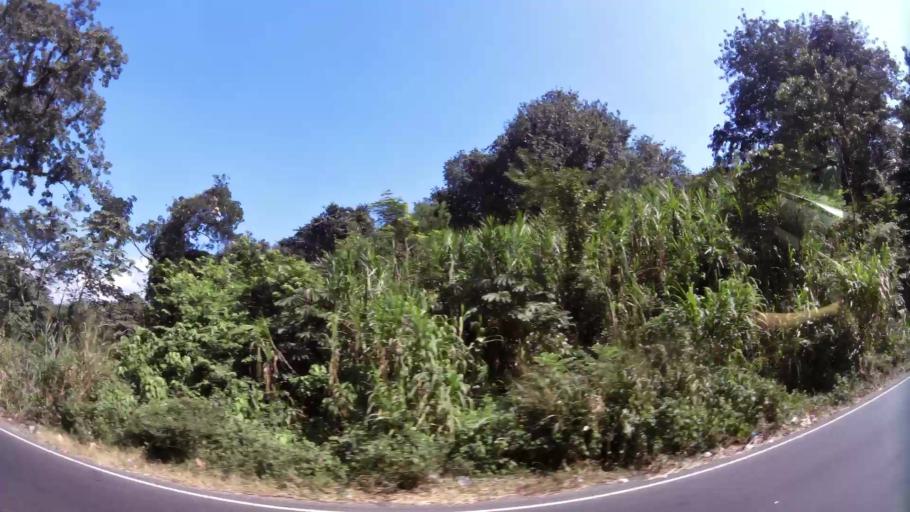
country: GT
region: Suchitepeque
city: Mazatenango
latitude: 14.5421
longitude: -91.4996
